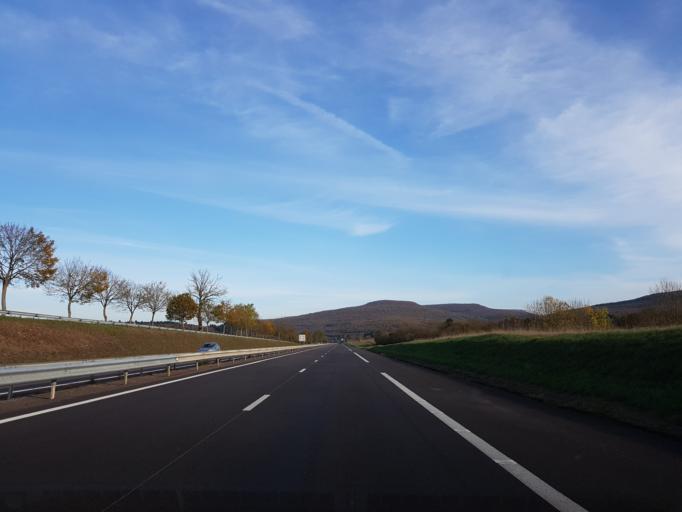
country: FR
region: Bourgogne
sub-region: Departement de la Cote-d'Or
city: Fleurey-sur-Ouche
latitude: 47.2998
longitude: 4.7869
